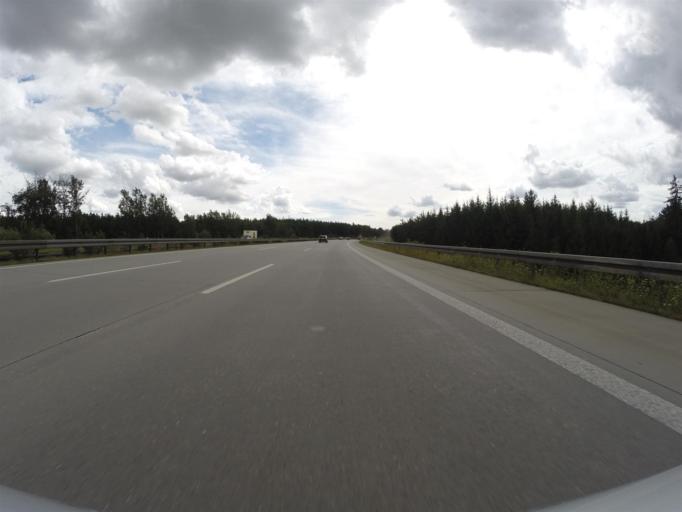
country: DE
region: Thuringia
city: Geroda
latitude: 50.7879
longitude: 11.8951
